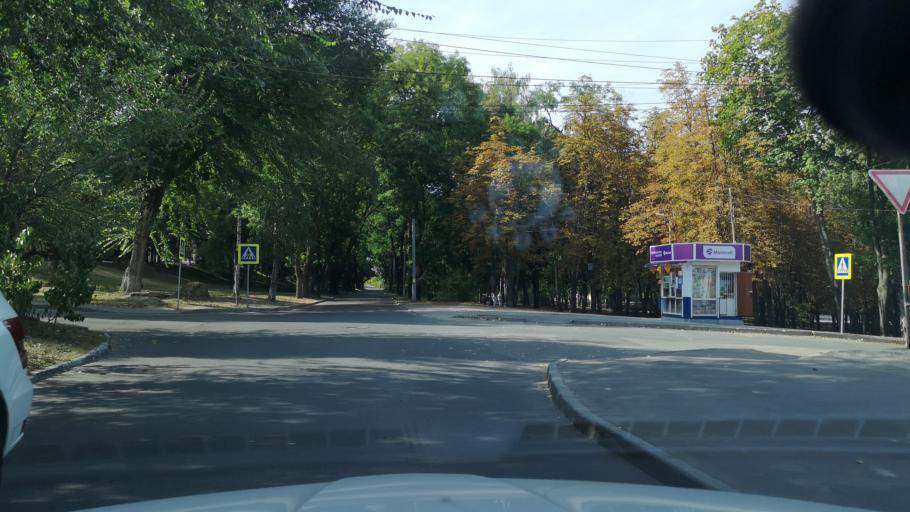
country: MD
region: Chisinau
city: Chisinau
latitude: 47.0351
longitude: 28.8043
